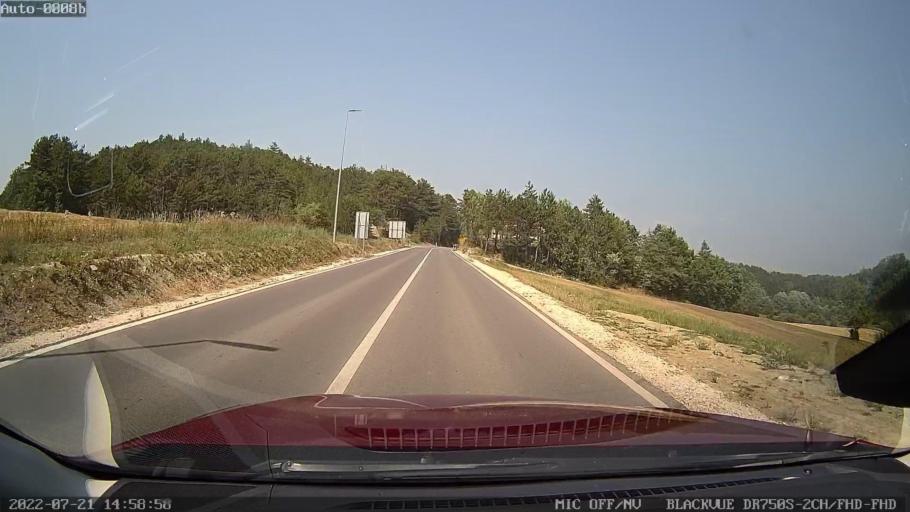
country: HR
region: Istarska
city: Pazin
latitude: 45.2163
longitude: 13.9574
